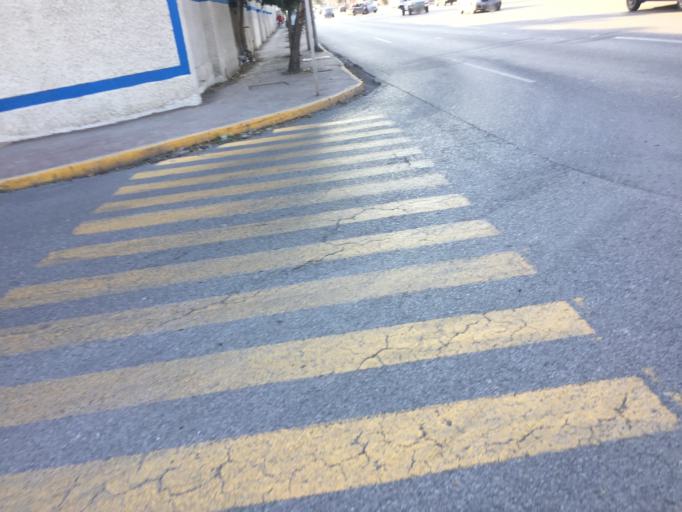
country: MX
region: Nuevo Leon
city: Garza Garcia
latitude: 25.6513
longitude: -100.3722
